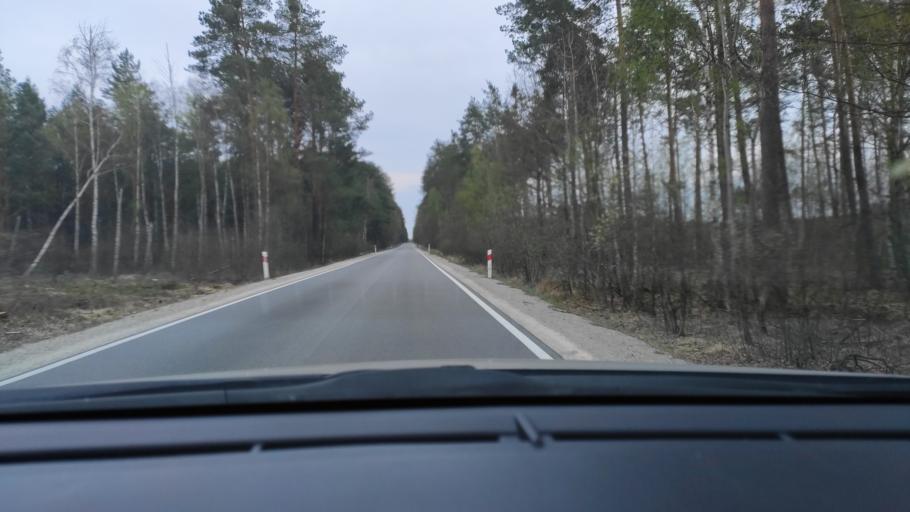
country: PL
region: Masovian Voivodeship
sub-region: Powiat zwolenski
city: Zwolen
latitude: 51.3950
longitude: 21.5440
